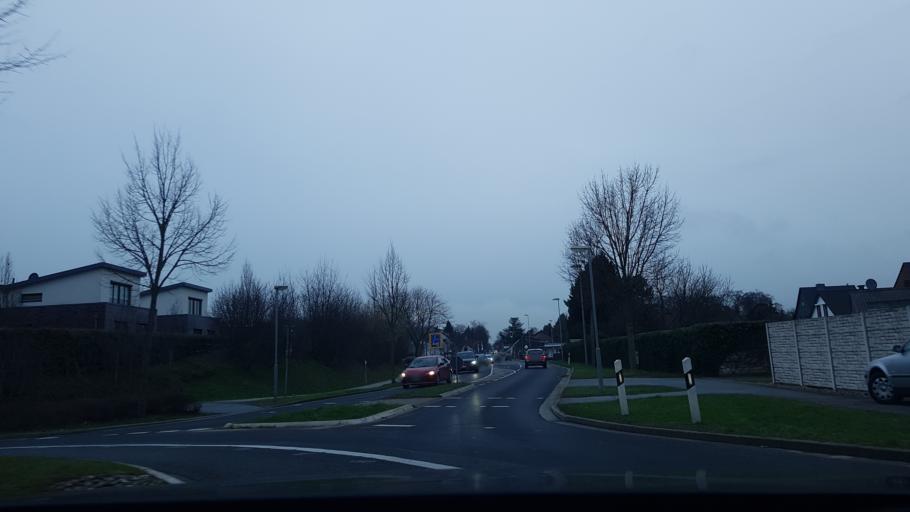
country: DE
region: North Rhine-Westphalia
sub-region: Regierungsbezirk Dusseldorf
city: Moers
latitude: 51.4192
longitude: 6.6560
